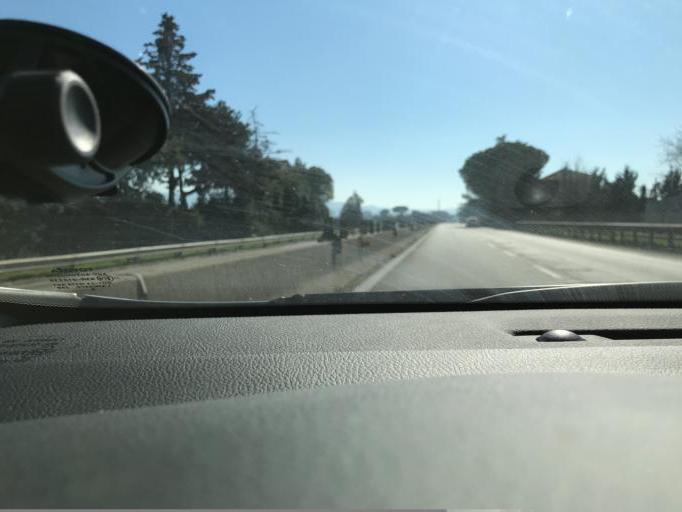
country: IT
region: Umbria
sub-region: Provincia di Perugia
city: San Martino in Campo
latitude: 43.0397
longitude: 12.4101
